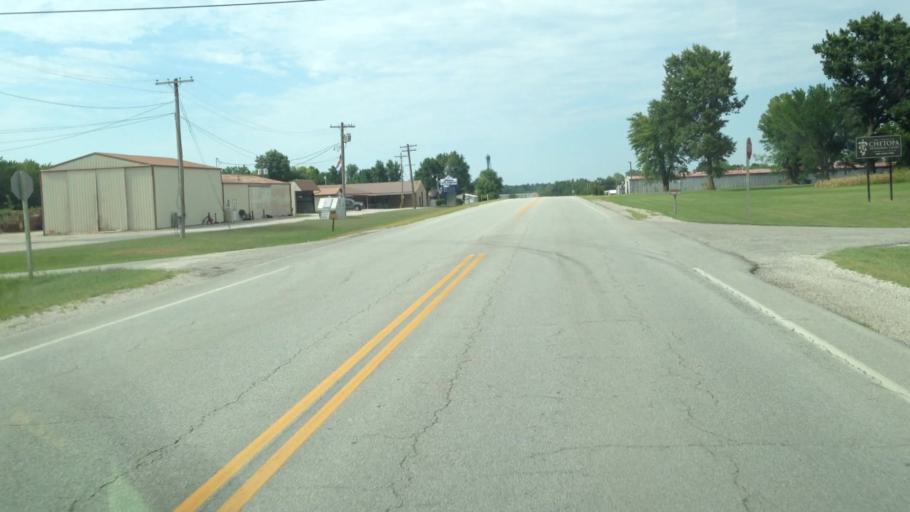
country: US
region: Kansas
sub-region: Labette County
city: Chetopa
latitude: 37.0416
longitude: -95.1002
